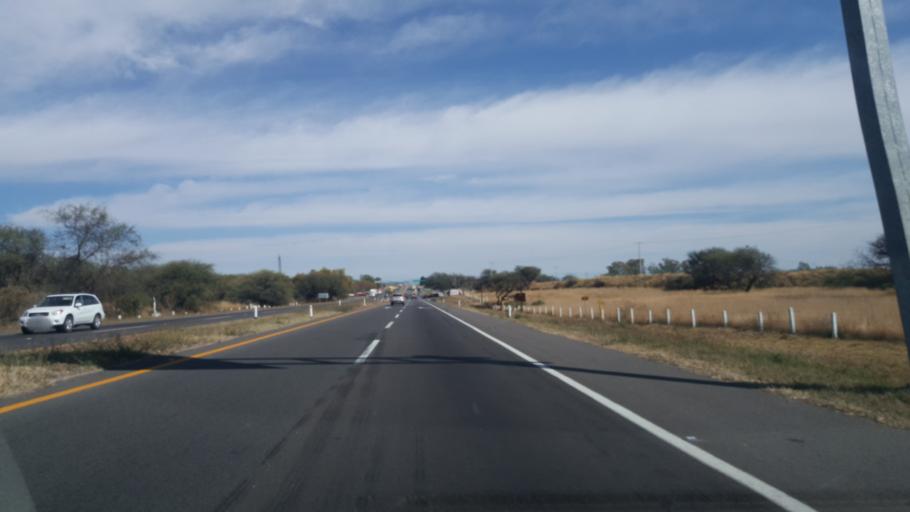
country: MX
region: Jalisco
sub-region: Lagos de Moreno
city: Cristeros [Fraccionamiento]
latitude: 21.3147
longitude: -102.0525
